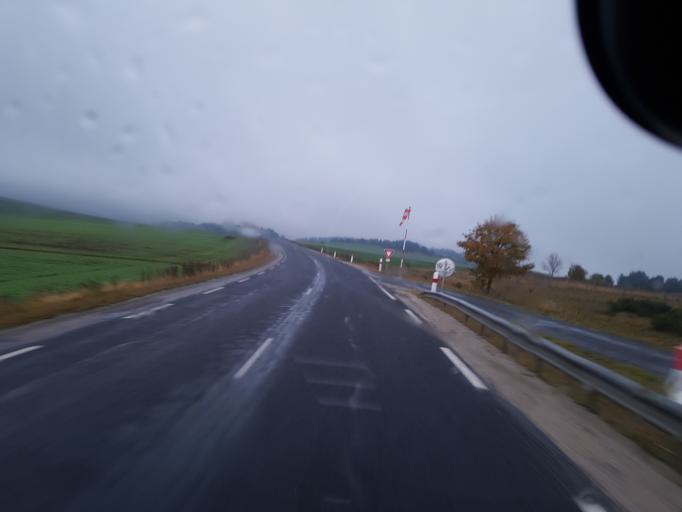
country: FR
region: Languedoc-Roussillon
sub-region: Departement de la Lozere
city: Langogne
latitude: 44.8362
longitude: 3.8602
